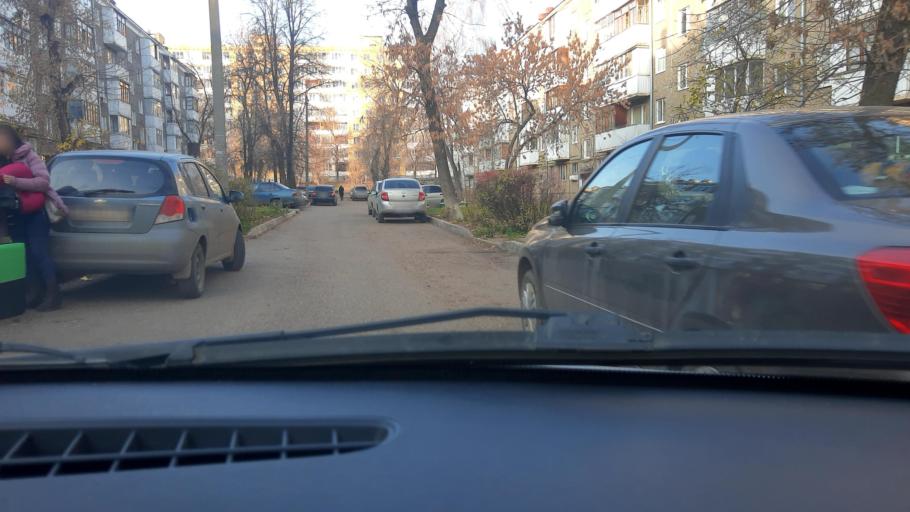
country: RU
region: Bashkortostan
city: Ufa
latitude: 54.8074
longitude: 56.1252
